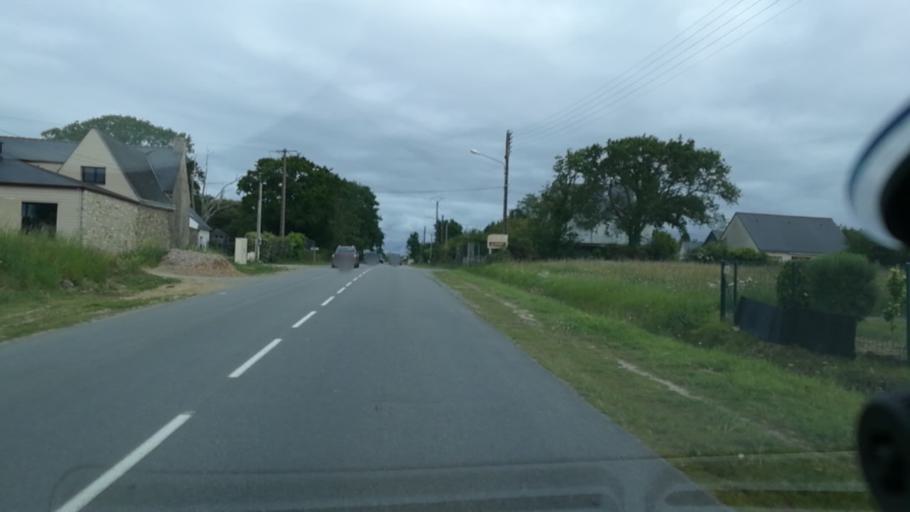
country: FR
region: Brittany
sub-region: Departement du Morbihan
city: Penestin
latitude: 47.4738
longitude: -2.4787
